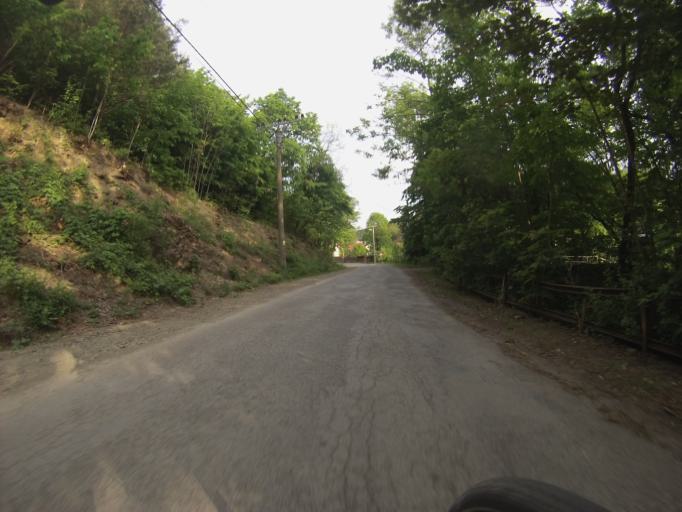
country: CZ
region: Olomoucky
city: Pteni
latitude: 49.4732
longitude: 16.9663
